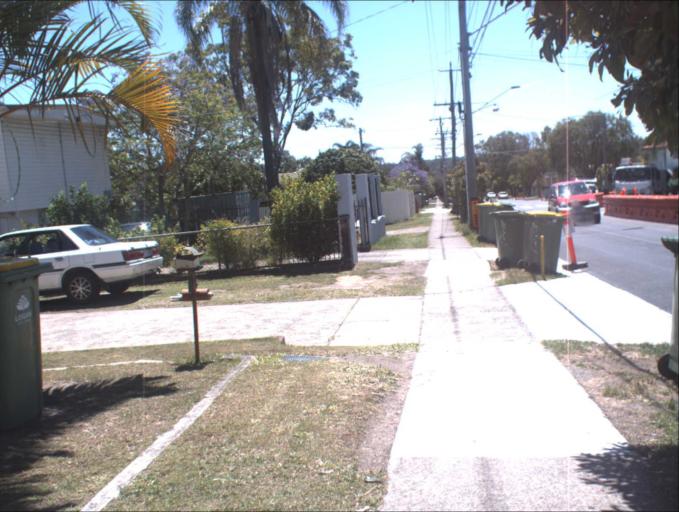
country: AU
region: Queensland
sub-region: Logan
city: Woodridge
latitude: -27.6246
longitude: 153.1103
